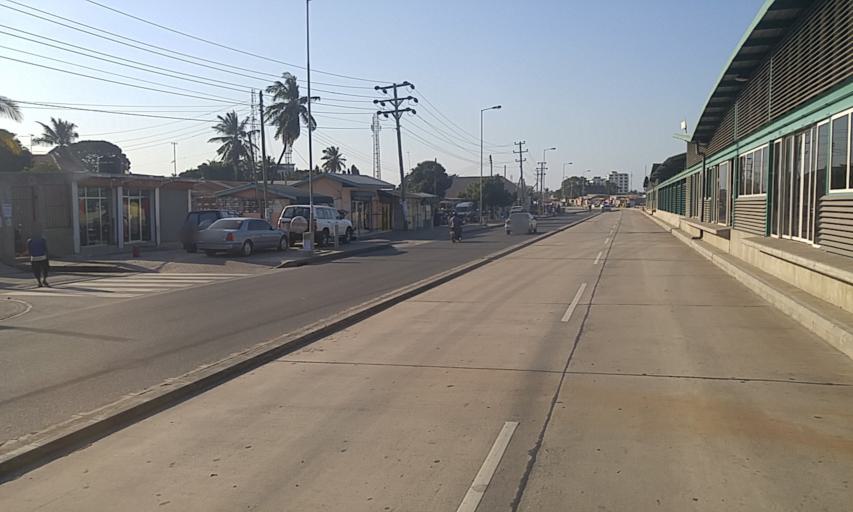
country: TZ
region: Dar es Salaam
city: Magomeni
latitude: -6.7959
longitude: 39.2640
